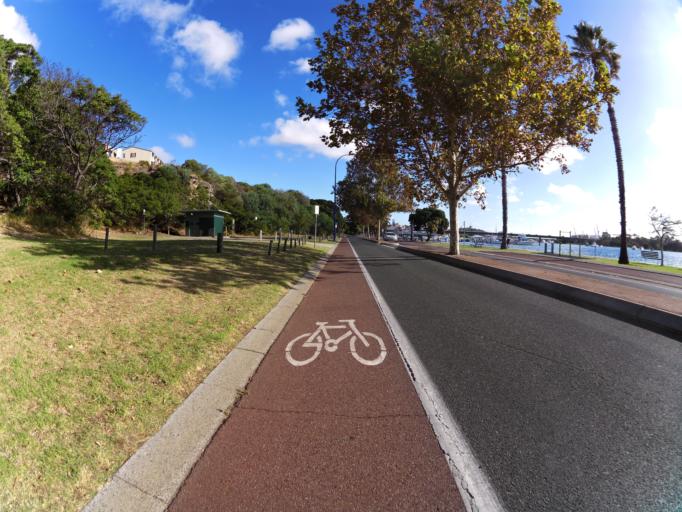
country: AU
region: Western Australia
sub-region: East Fremantle
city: East Fremantle
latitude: -32.0359
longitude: 115.7628
